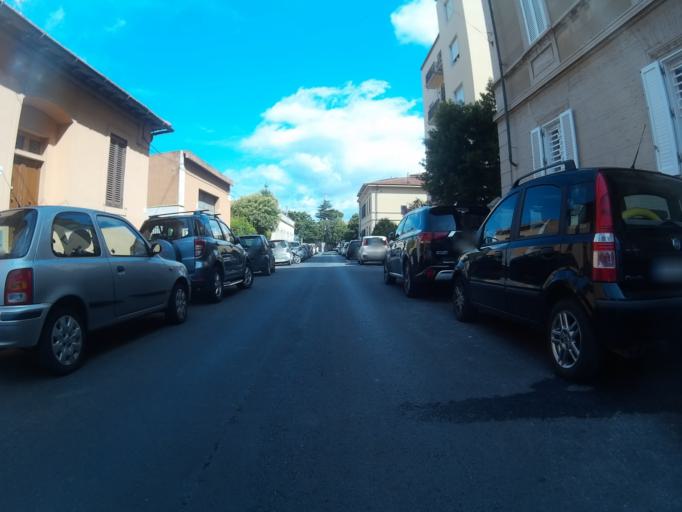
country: IT
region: Tuscany
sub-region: Provincia di Livorno
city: Livorno
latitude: 43.5440
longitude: 10.3208
